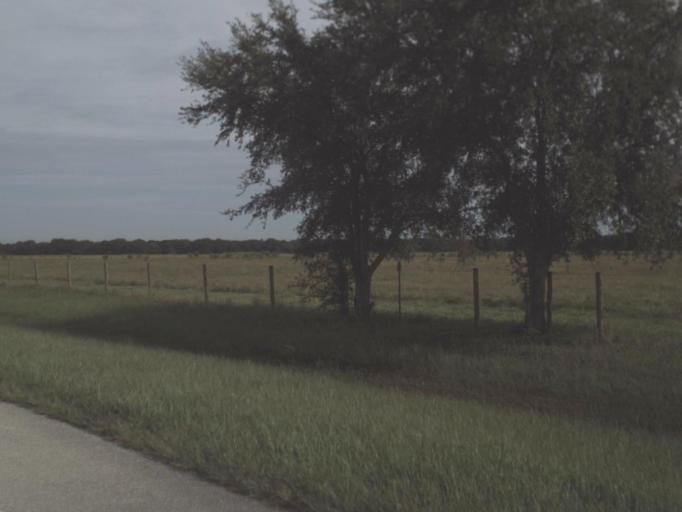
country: US
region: Florida
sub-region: DeSoto County
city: Nocatee
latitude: 27.0431
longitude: -81.7782
